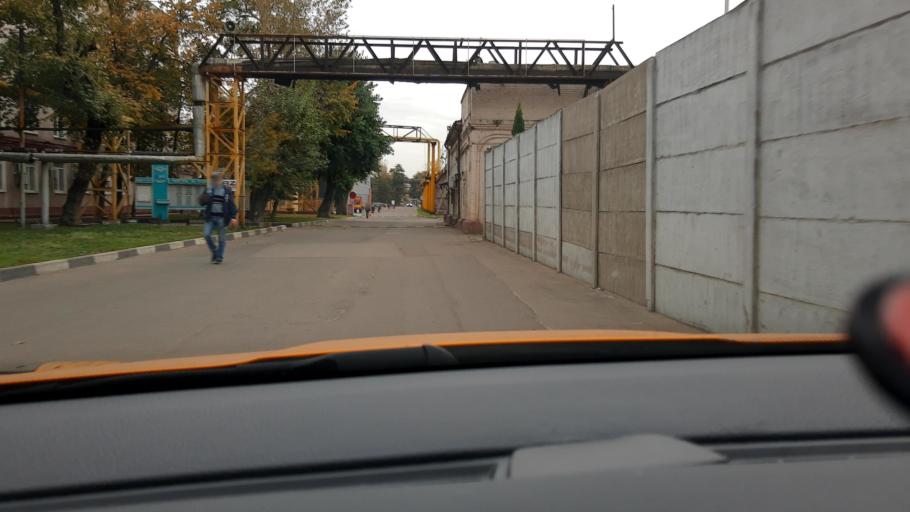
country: RU
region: Moscow
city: Taganskiy
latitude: 55.7220
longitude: 37.6826
